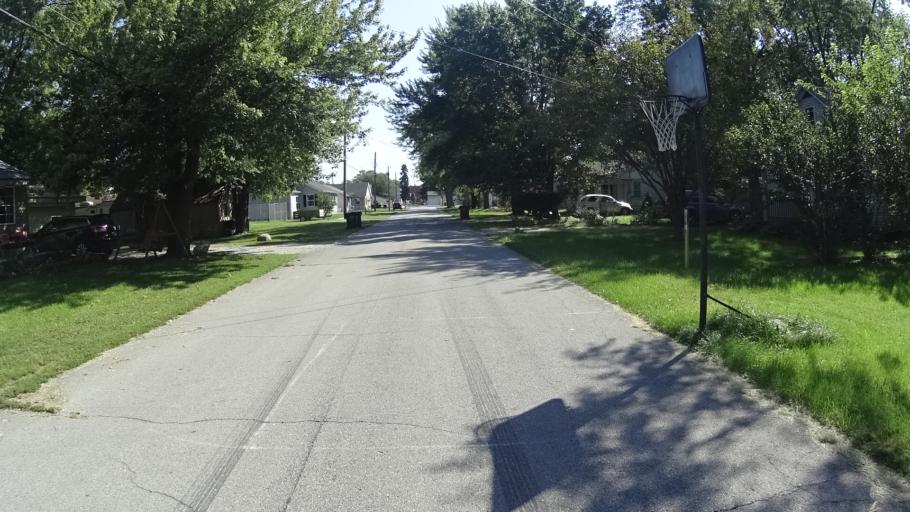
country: US
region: Indiana
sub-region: Madison County
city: Lapel
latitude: 40.0669
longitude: -85.8524
